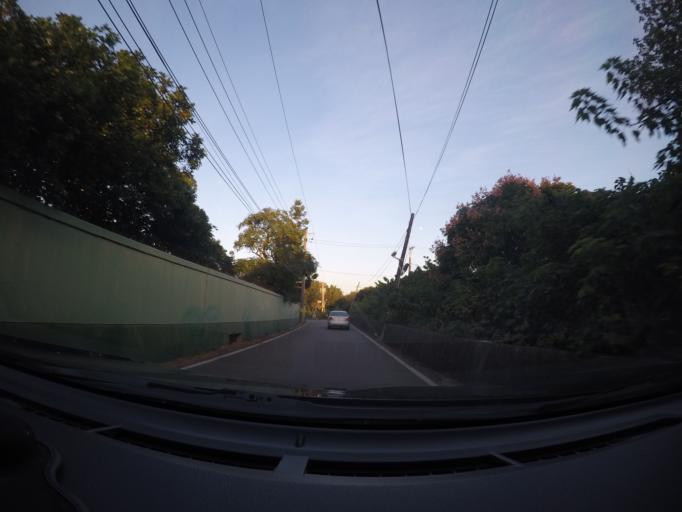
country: TW
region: Taiwan
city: Taoyuan City
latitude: 25.0009
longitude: 121.2537
